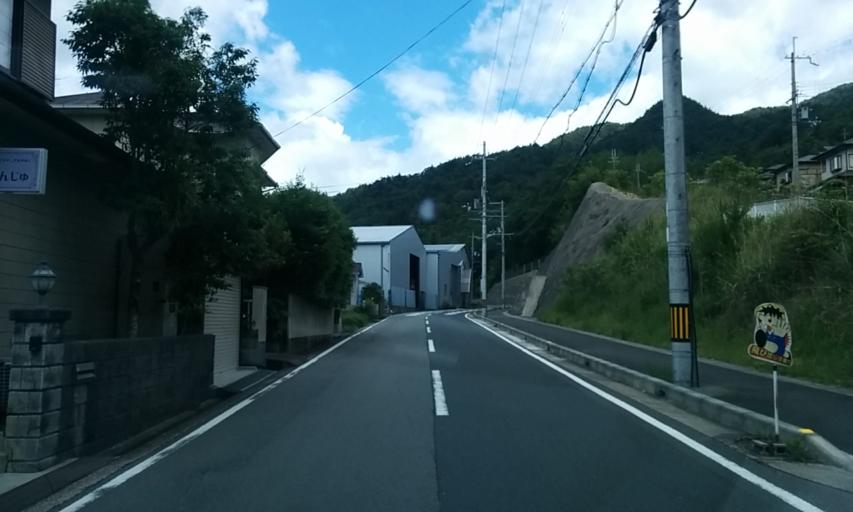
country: JP
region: Kyoto
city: Kameoka
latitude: 35.0159
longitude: 135.4231
